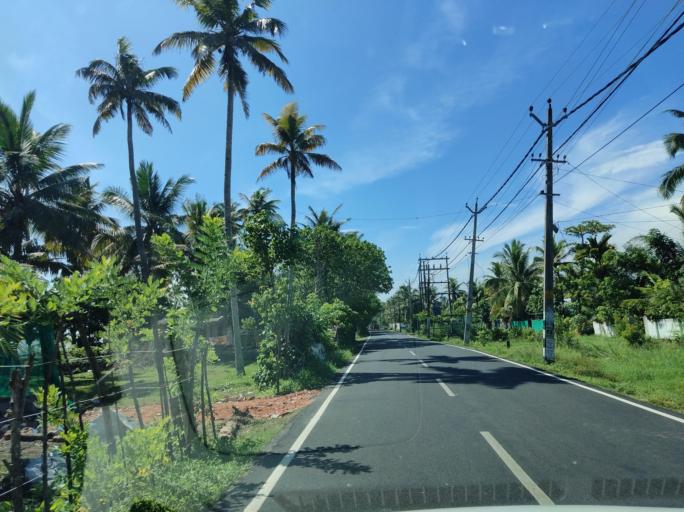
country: IN
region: Kerala
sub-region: Alappuzha
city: Kayankulam
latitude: 9.1711
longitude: 76.4478
